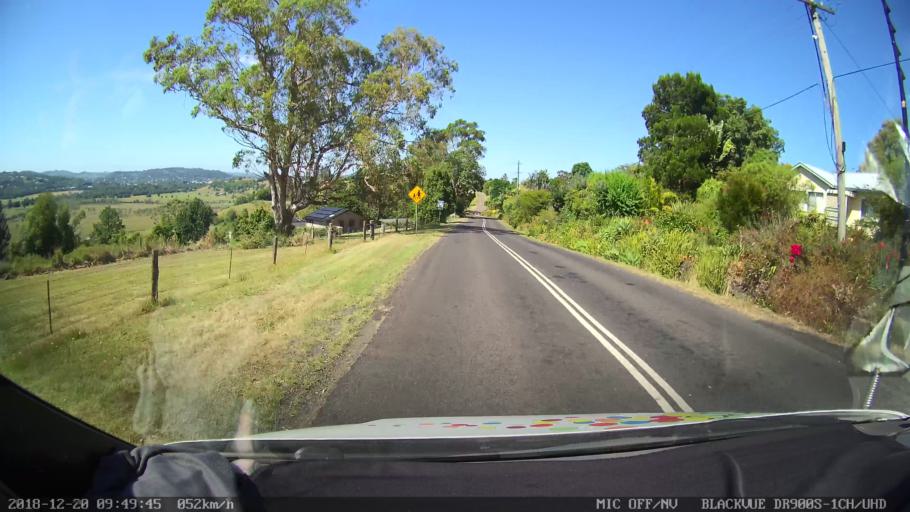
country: AU
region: New South Wales
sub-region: Lismore Municipality
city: Lismore
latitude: -28.7750
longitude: 153.2831
